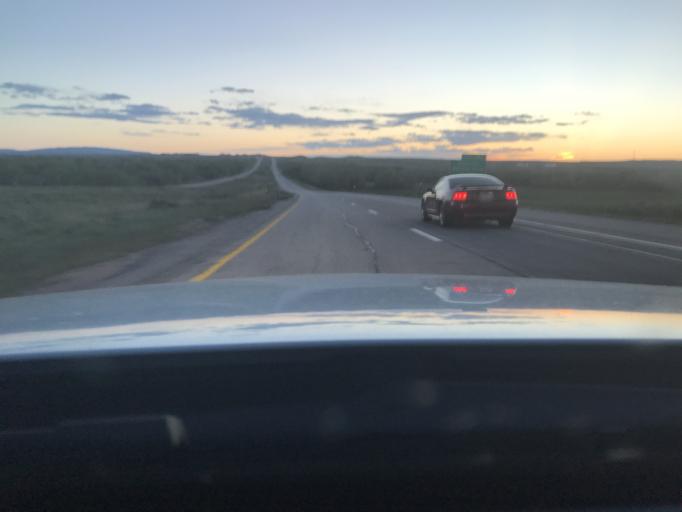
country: US
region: Wyoming
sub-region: Converse County
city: Glenrock
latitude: 42.8373
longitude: -105.8608
